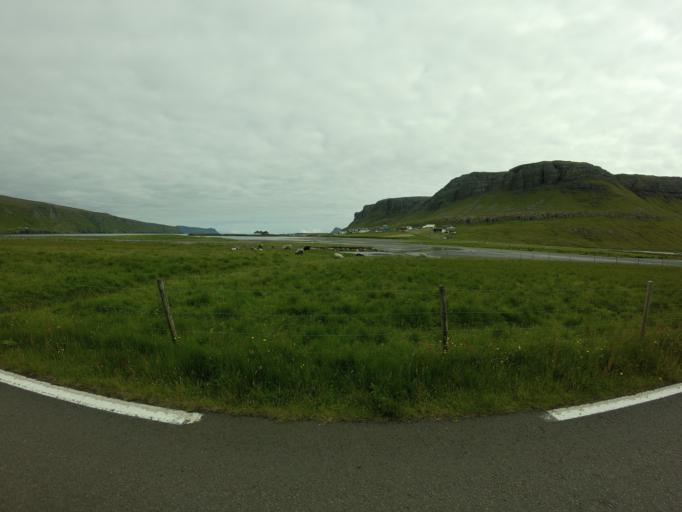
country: FO
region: Suduroy
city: Tvoroyri
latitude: 61.5907
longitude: -6.9416
